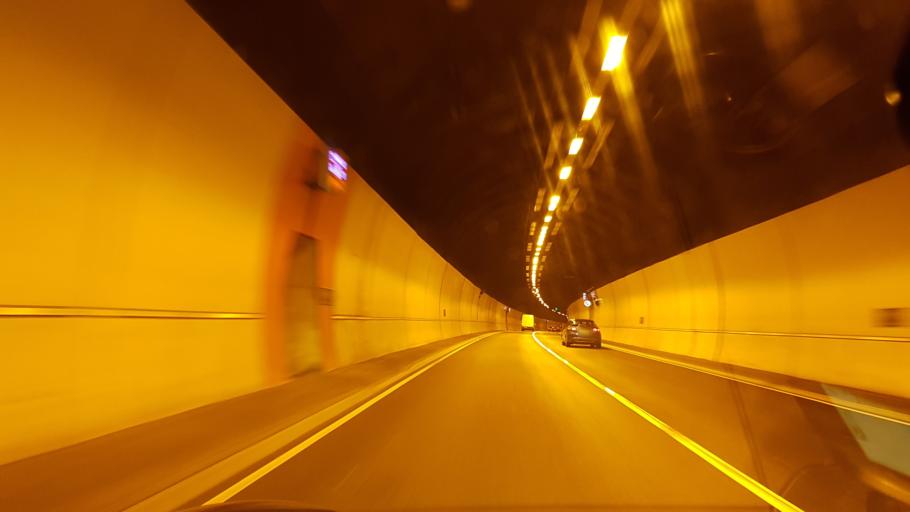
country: GB
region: England
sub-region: Surrey
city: Hindhead
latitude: 51.1191
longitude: -0.7161
